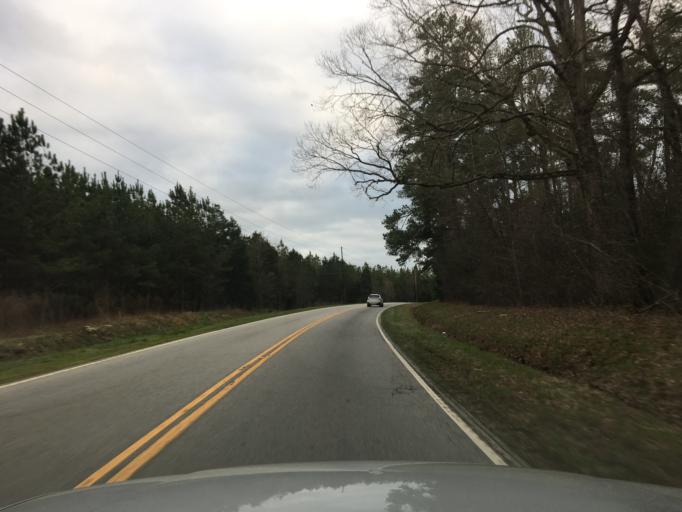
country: US
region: South Carolina
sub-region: Saluda County
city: Saluda
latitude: 33.9844
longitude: -81.7694
